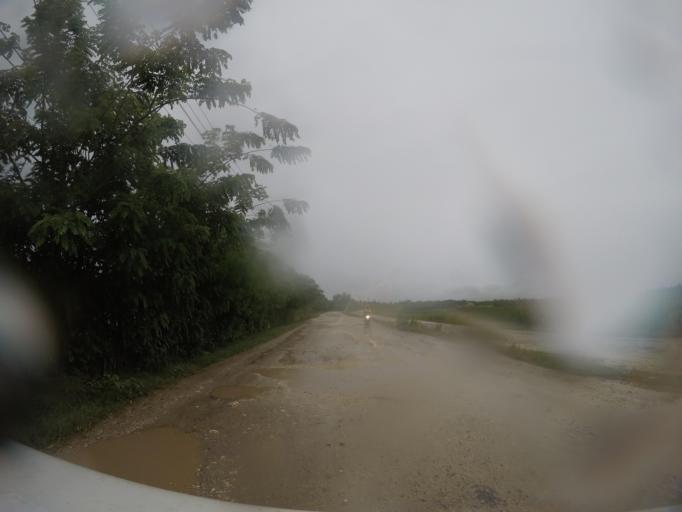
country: TL
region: Lautem
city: Lospalos
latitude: -8.5097
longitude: 127.0048
